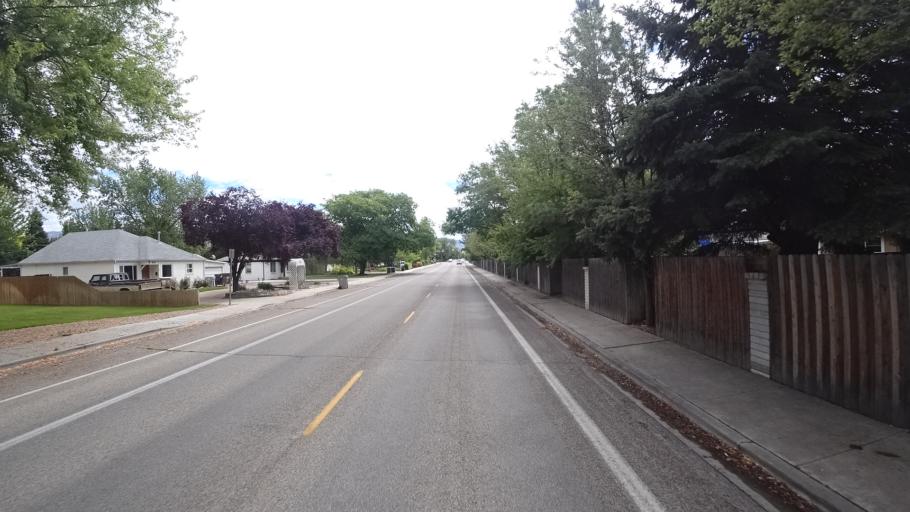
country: US
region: Idaho
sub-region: Ada County
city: Boise
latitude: 43.5789
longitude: -116.1860
